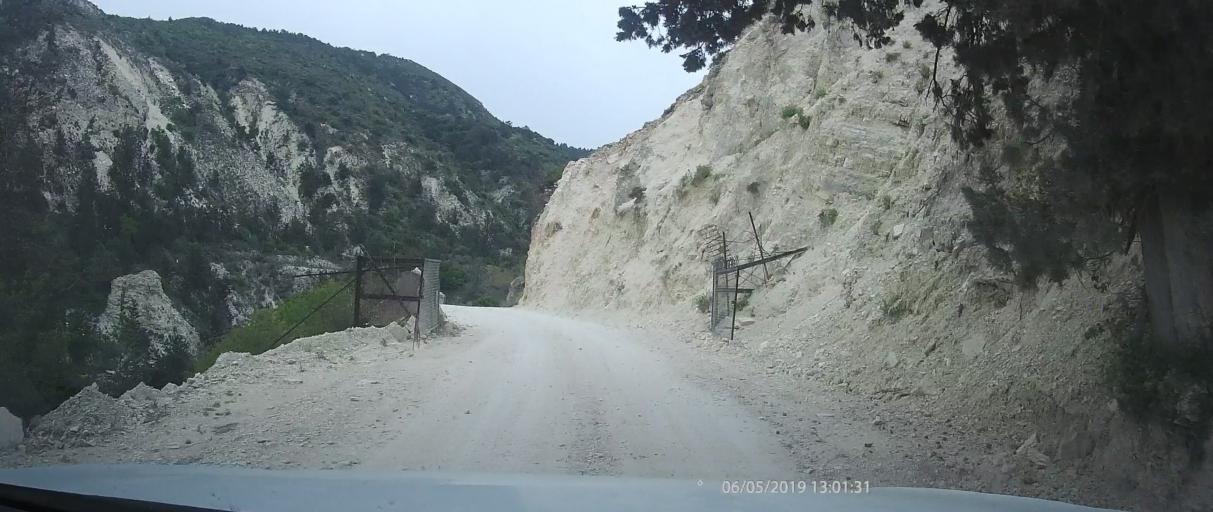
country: CY
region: Pafos
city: Tala
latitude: 34.8695
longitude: 32.4335
